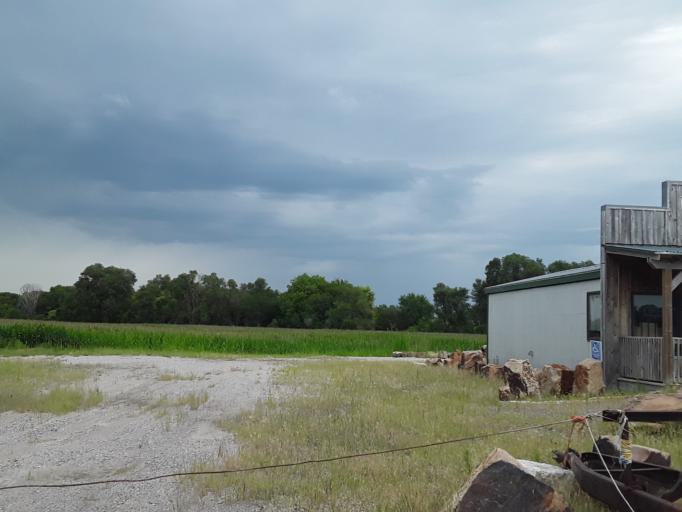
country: US
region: Nebraska
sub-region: Saunders County
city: Yutan
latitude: 41.2339
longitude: -96.3989
